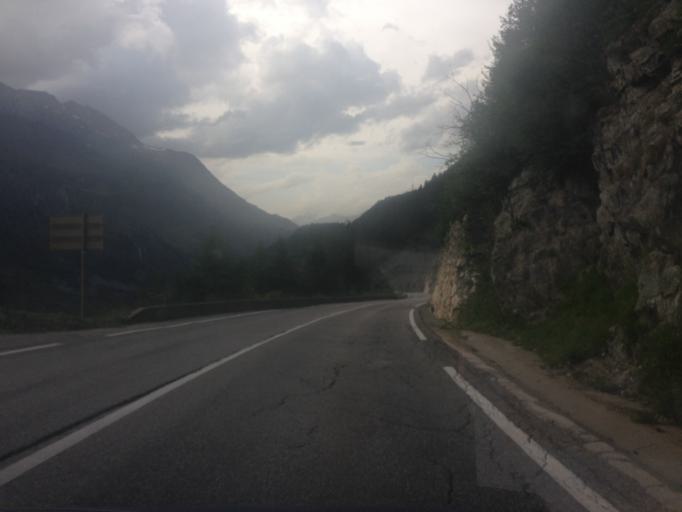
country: FR
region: Rhone-Alpes
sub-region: Departement de la Savoie
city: Tignes
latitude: 45.5001
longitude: 6.9312
